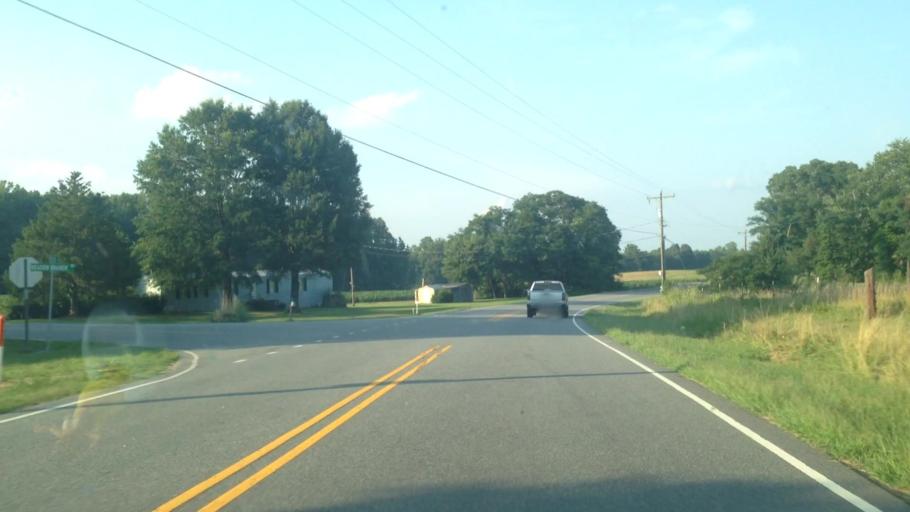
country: US
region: North Carolina
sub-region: Rockingham County
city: Reidsville
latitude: 36.2868
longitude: -79.7508
